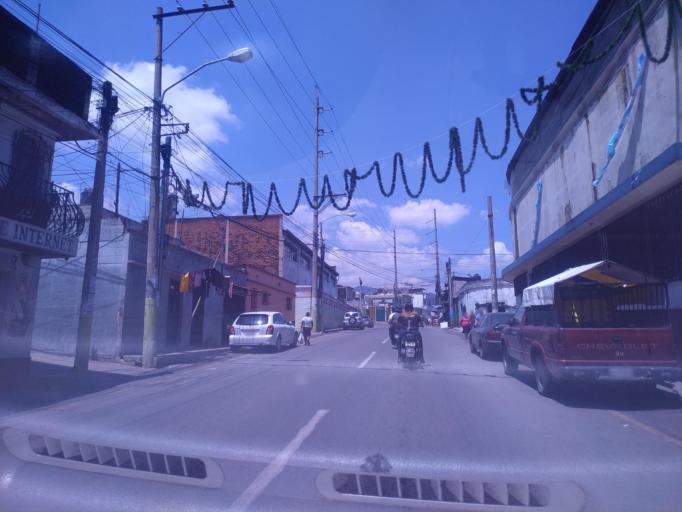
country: GT
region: Guatemala
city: Mixco
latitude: 14.6779
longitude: -90.5708
